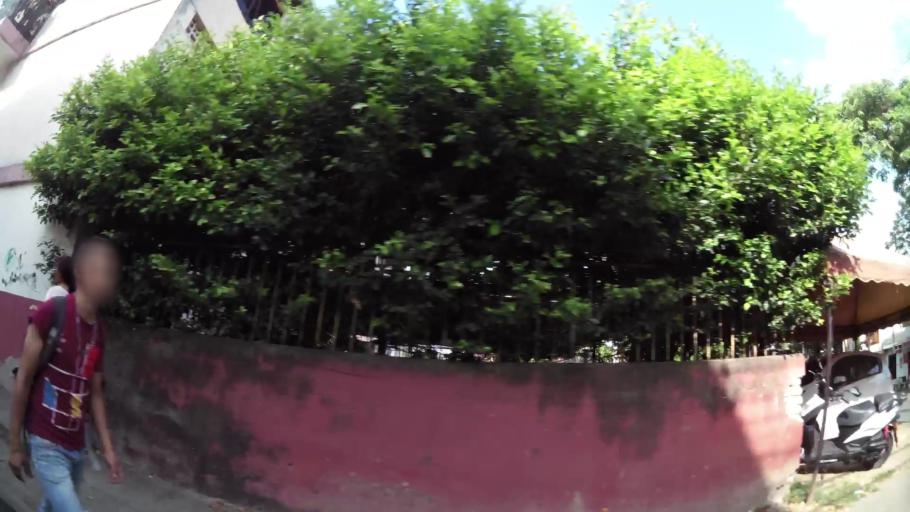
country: CO
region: Valle del Cauca
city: Cali
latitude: 3.4674
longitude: -76.5149
